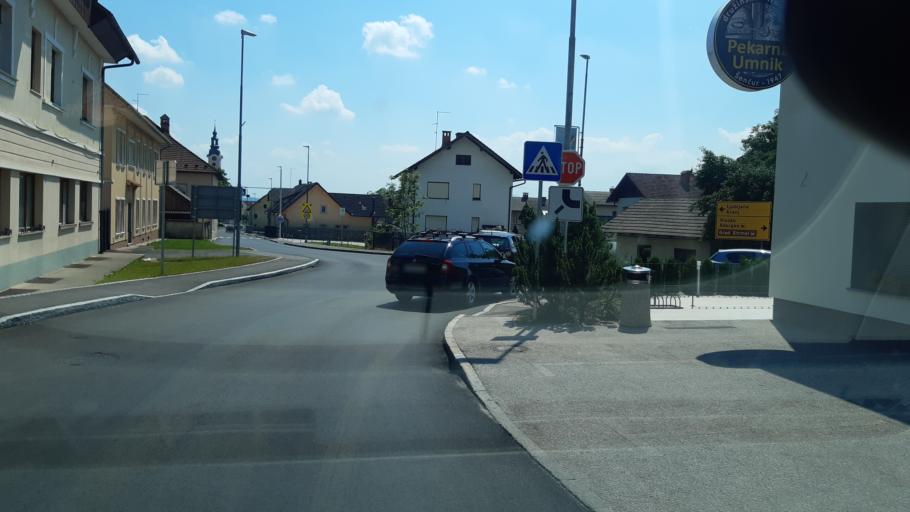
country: SI
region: Cerklje na Gorenjskem
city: Cerklje na Gorenjskem
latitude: 46.2562
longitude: 14.4881
